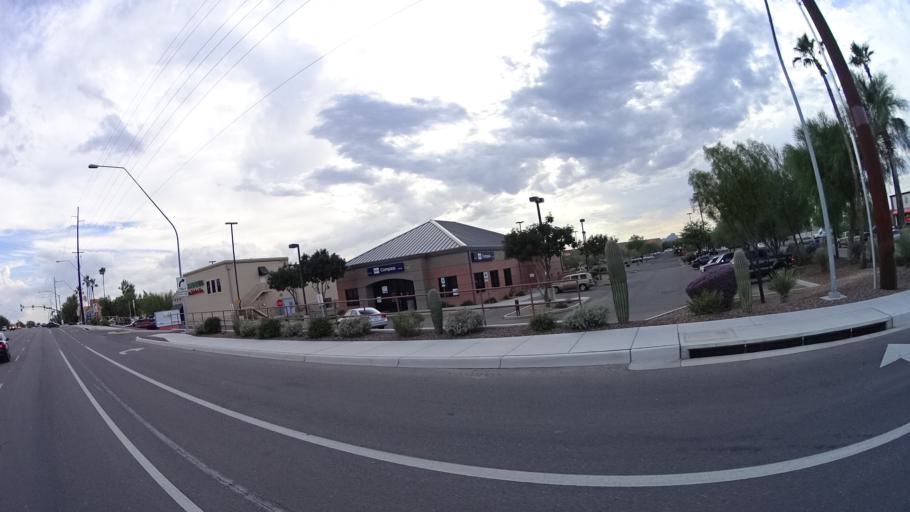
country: US
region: Arizona
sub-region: Pima County
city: Casas Adobes
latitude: 32.3451
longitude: -111.0129
